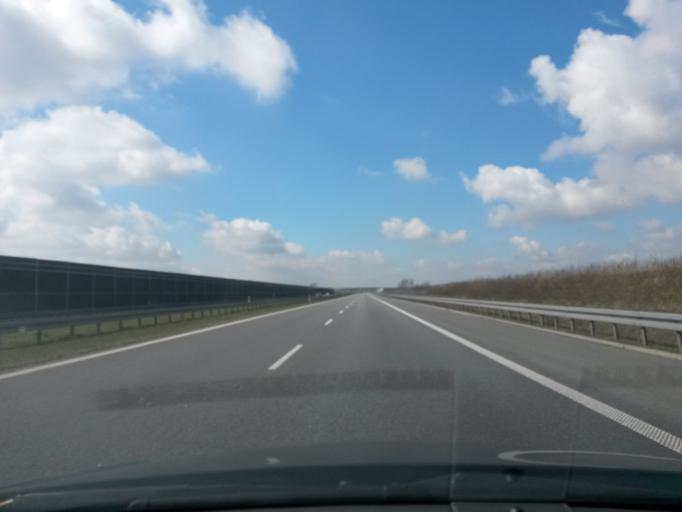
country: PL
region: Masovian Voivodeship
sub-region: Powiat zyrardowski
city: Guzow
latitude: 52.0736
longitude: 20.2736
